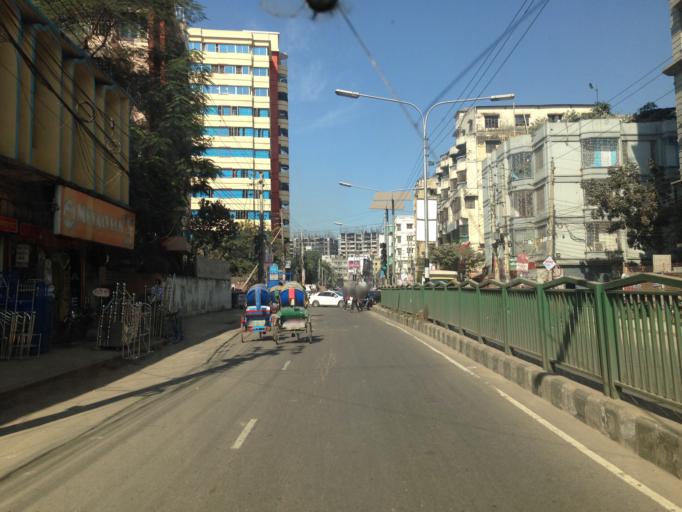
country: BD
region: Dhaka
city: Azimpur
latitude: 23.8089
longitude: 90.3613
